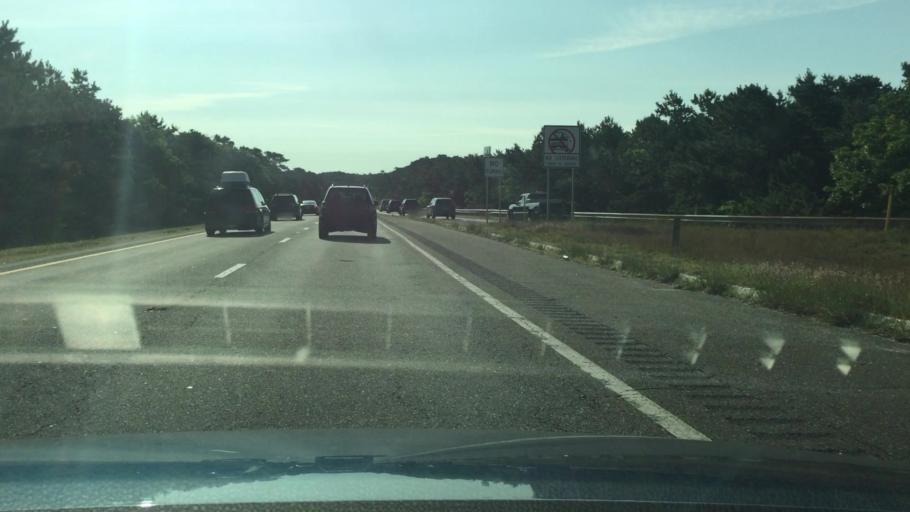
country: US
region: Massachusetts
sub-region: Barnstable County
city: Yarmouth Port
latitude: 41.6868
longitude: -70.2541
